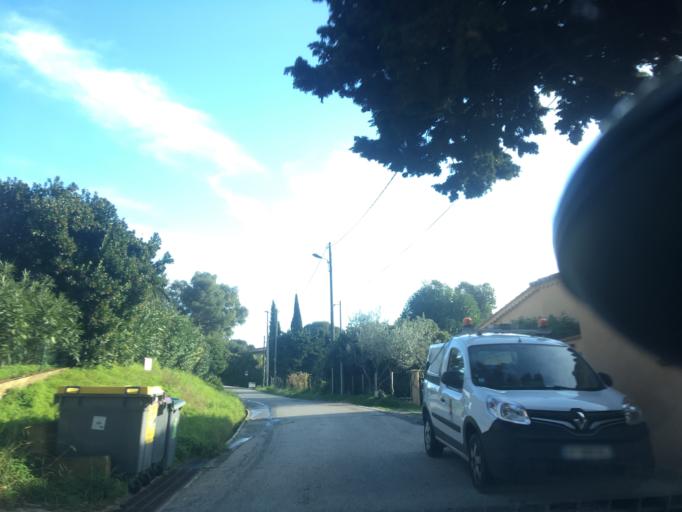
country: FR
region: Provence-Alpes-Cote d'Azur
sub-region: Departement du Var
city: Cavalaire-sur-Mer
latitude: 43.1582
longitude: 6.4764
